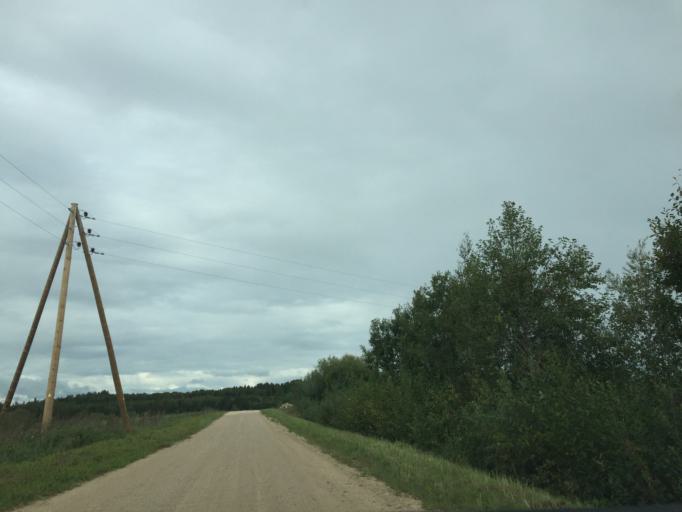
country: LV
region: Pargaujas
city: Stalbe
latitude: 57.5157
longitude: 24.9171
